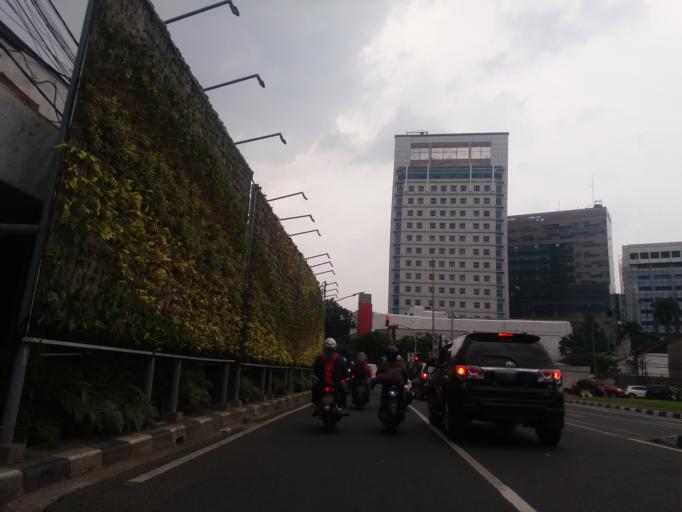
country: ID
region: Jakarta Raya
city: Jakarta
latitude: -6.1832
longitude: 106.8342
